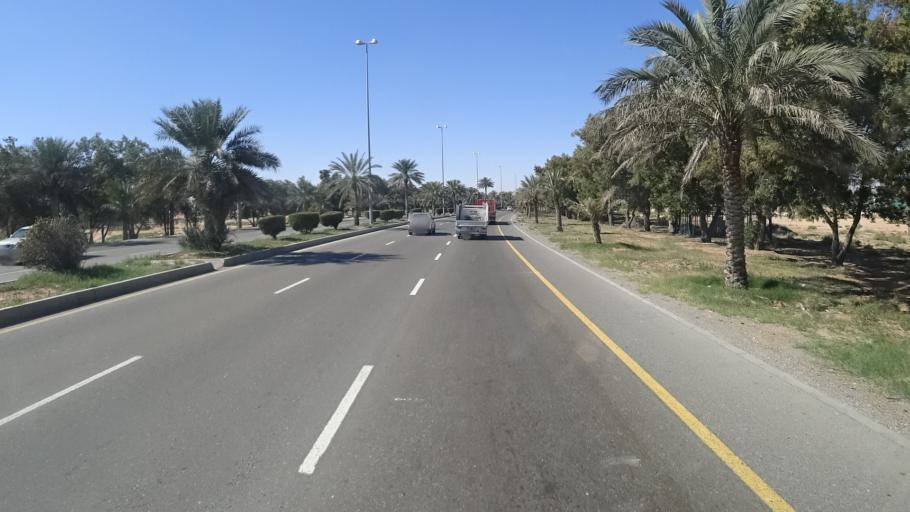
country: AE
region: Abu Dhabi
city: Al Ain
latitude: 24.0875
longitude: 55.6842
